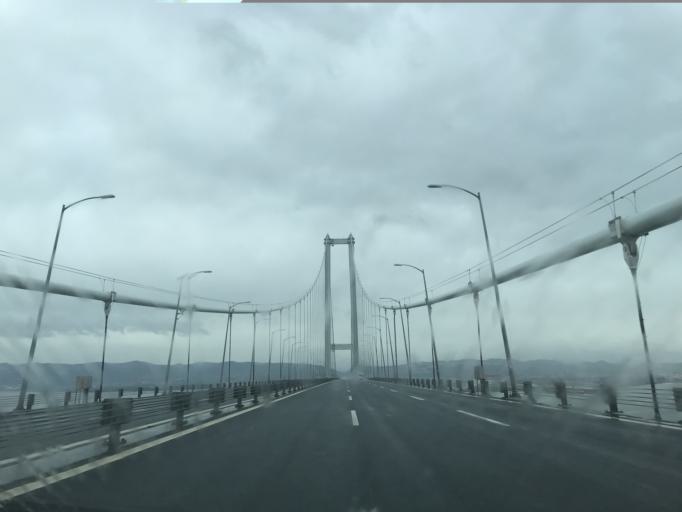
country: TR
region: Kocaeli
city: Tavsancil
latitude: 40.7545
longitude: 29.5157
